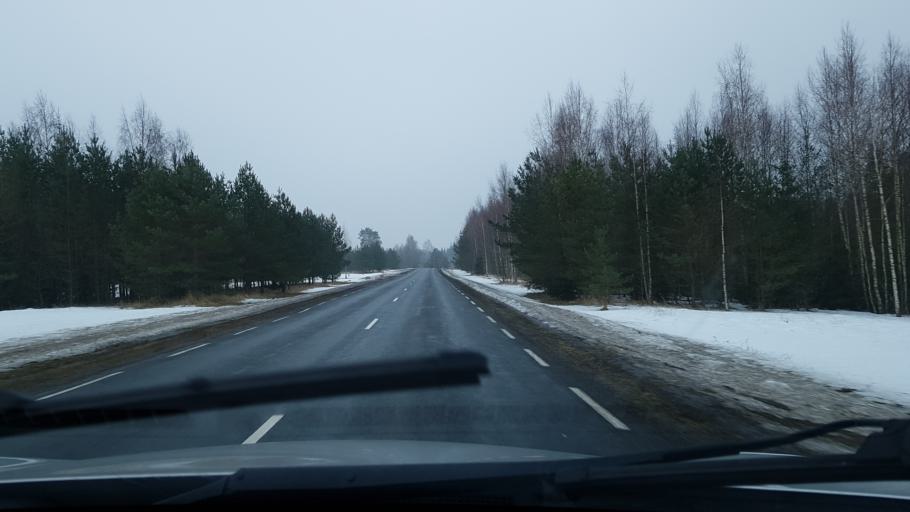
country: EE
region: Valgamaa
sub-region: Torva linn
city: Torva
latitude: 58.1248
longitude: 25.9926
